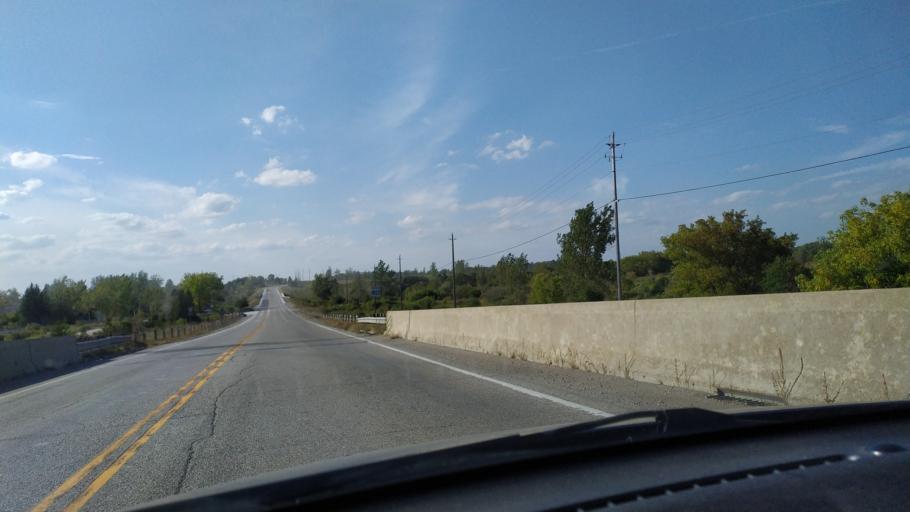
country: CA
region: Ontario
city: Ingersoll
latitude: 43.0695
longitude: -80.8495
